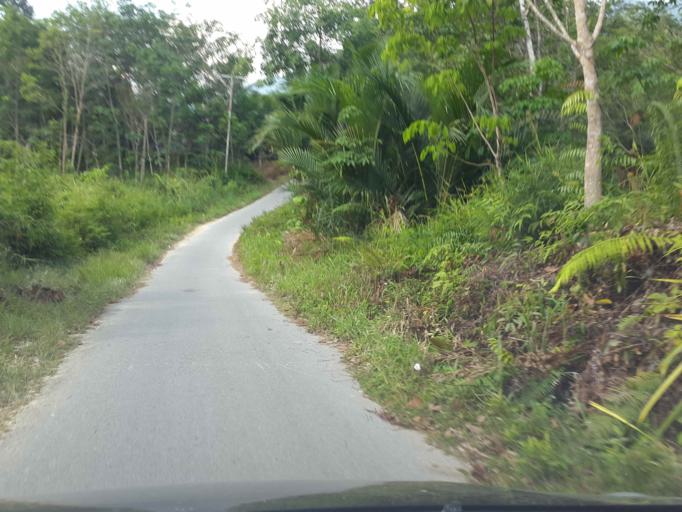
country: MY
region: Sarawak
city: Kuching
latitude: 1.6825
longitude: 109.5897
